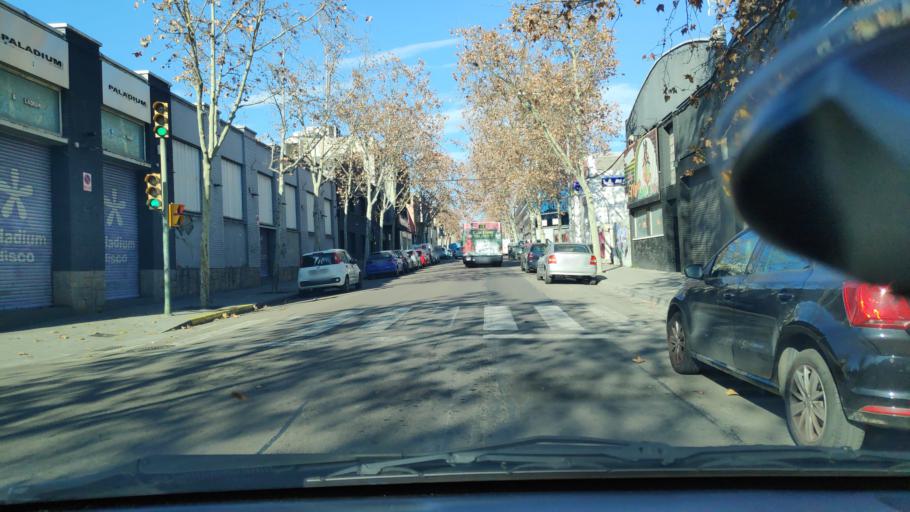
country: ES
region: Catalonia
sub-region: Provincia de Barcelona
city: Sabadell
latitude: 41.5342
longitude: 2.0994
